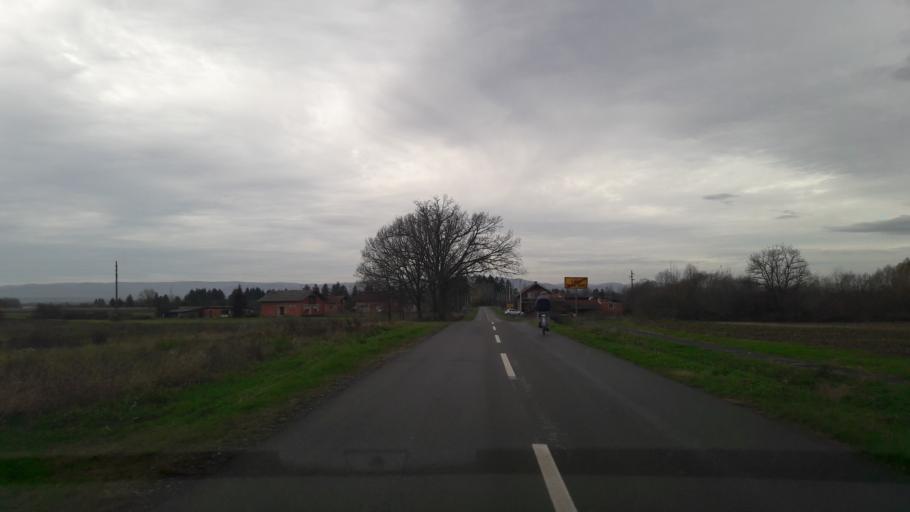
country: HR
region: Osjecko-Baranjska
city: Martin
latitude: 45.5320
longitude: 18.0570
